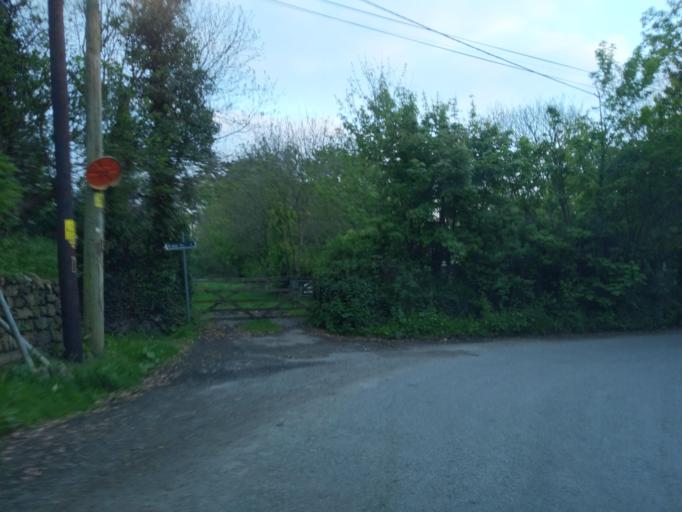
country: GB
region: England
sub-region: Cornwall
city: Polzeath
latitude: 50.5576
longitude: -4.8827
